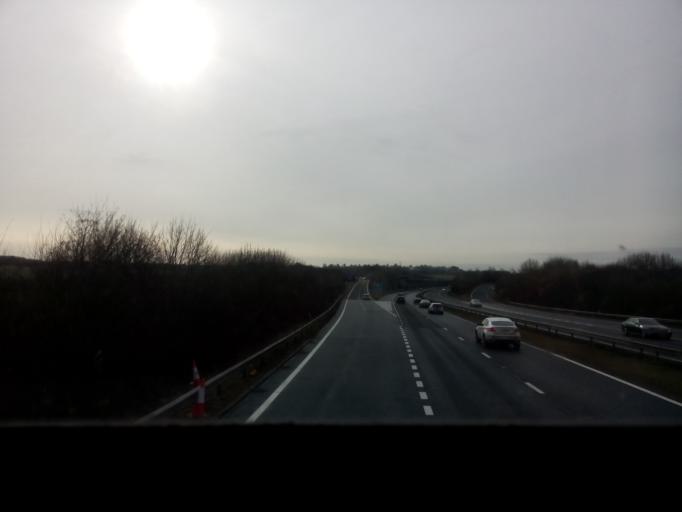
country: GB
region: England
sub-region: Hampshire
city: Kings Worthy
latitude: 51.0759
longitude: -1.2929
